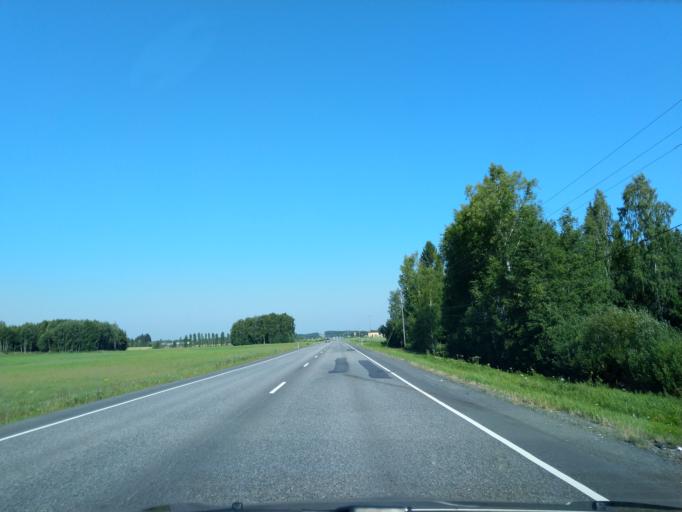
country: FI
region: Pirkanmaa
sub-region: Lounais-Pirkanmaa
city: Punkalaidun
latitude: 61.0335
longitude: 23.0173
